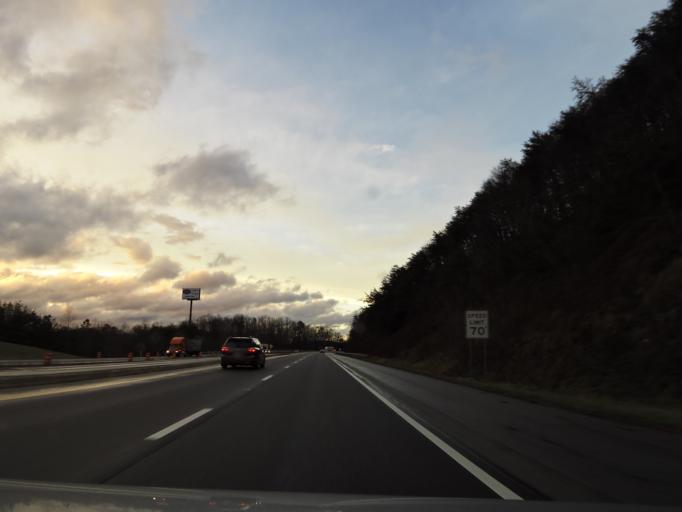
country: US
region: Tennessee
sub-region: Campbell County
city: Jacksboro
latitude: 36.3835
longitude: -84.2513
